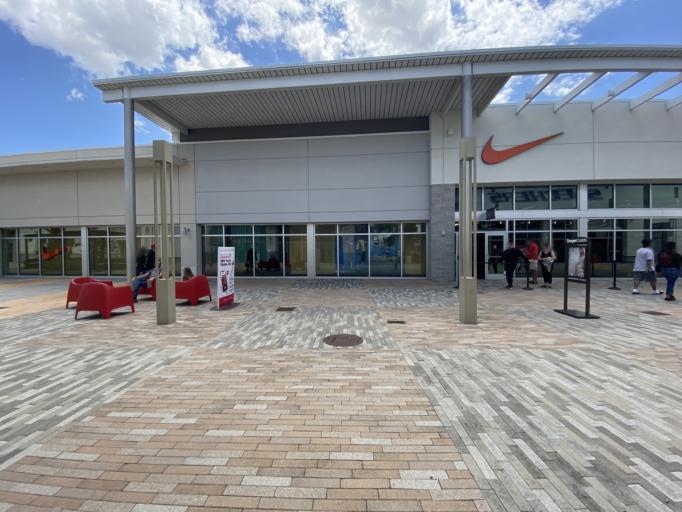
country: US
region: Florida
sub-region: Volusia County
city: Holly Hill
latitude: 29.2124
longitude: -81.0991
